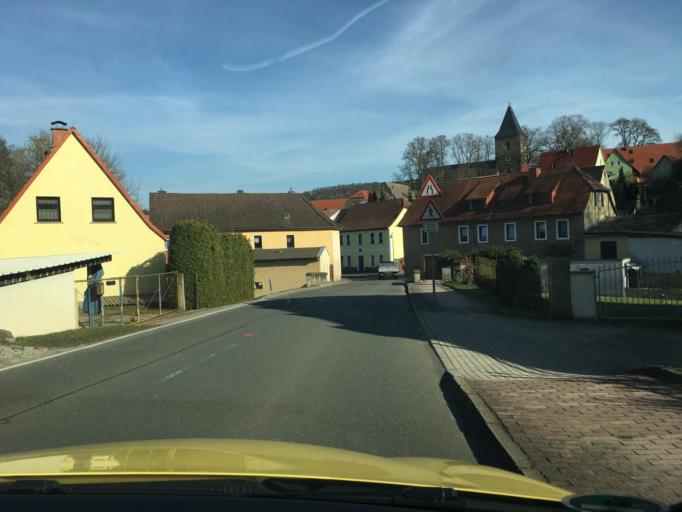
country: DE
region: Saxony-Anhalt
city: Bad Bibra
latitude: 51.2063
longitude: 11.5780
